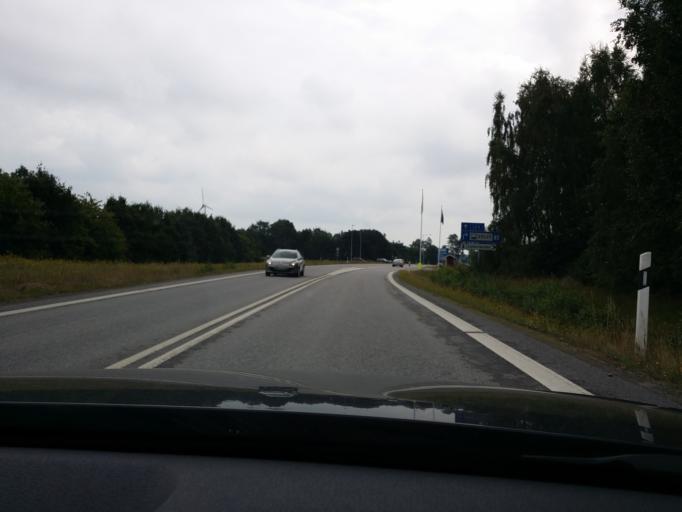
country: SE
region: Blekinge
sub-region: Solvesborgs Kommun
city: Soelvesborg
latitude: 56.0643
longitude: 14.6240
